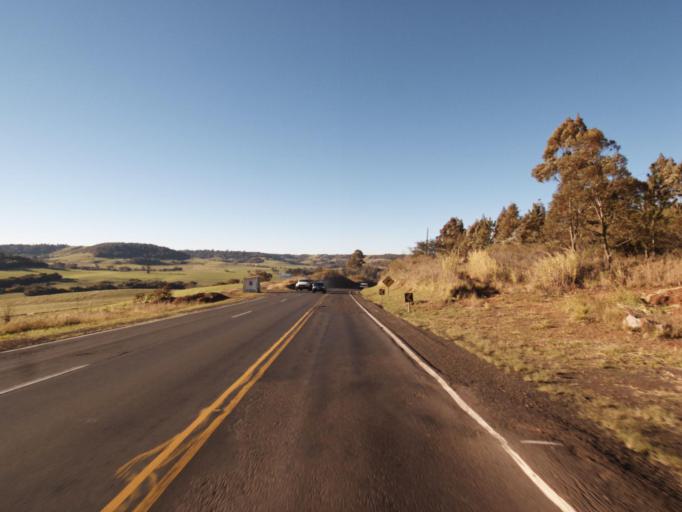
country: AR
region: Misiones
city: Bernardo de Irigoyen
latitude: -26.3281
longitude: -53.5453
